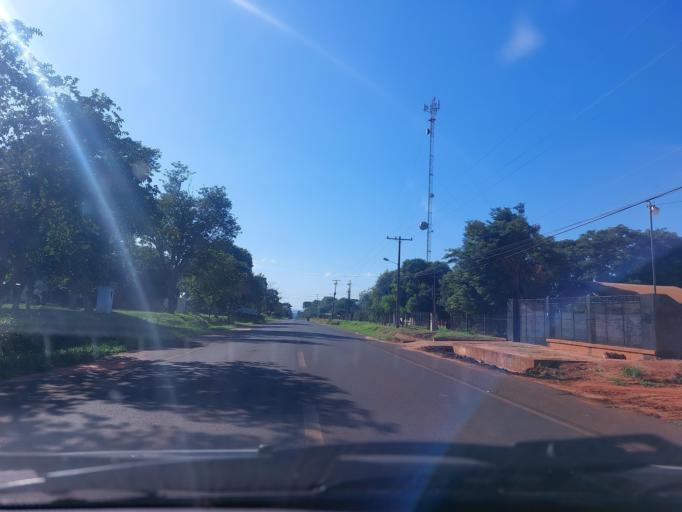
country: PY
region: San Pedro
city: Guayaybi
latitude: -24.5315
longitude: -56.4433
